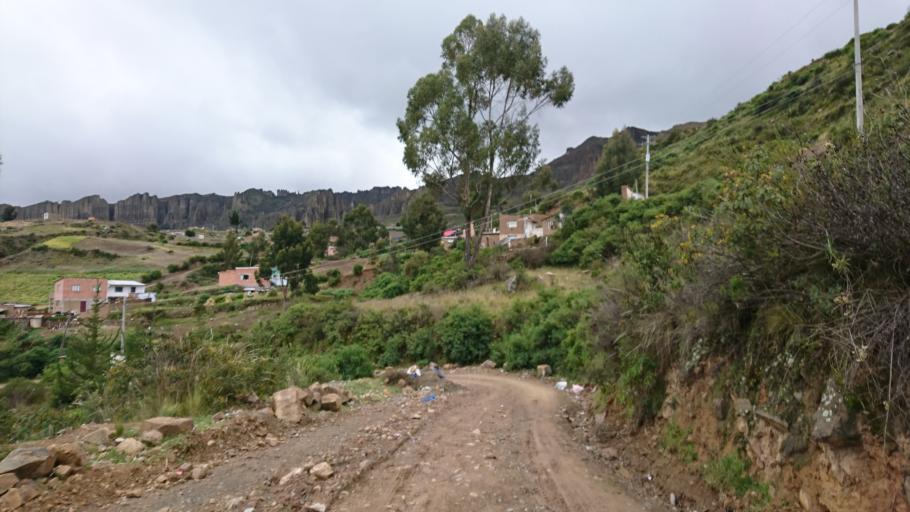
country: BO
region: La Paz
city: La Paz
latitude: -16.5467
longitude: -67.9940
